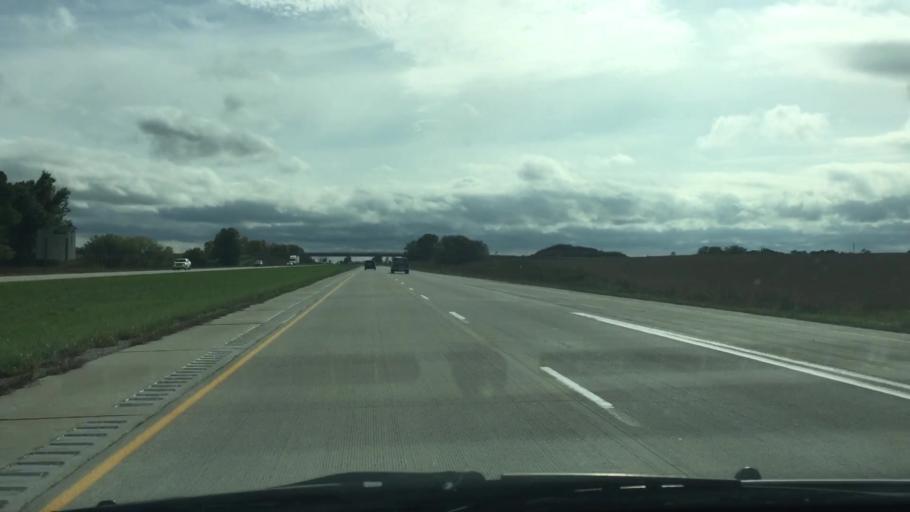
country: US
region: Iowa
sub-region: Decatur County
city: Leon
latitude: 40.8069
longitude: -93.8296
